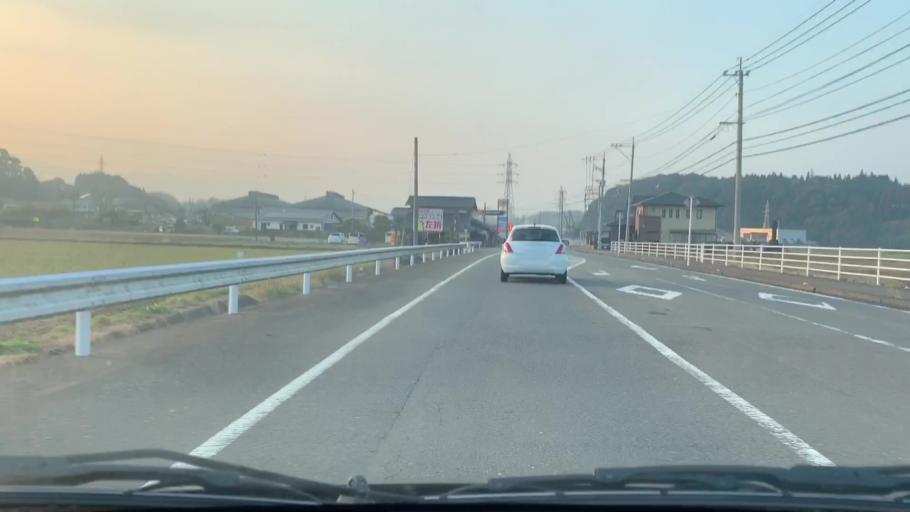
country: JP
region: Saga Prefecture
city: Imaricho-ko
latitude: 33.2687
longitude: 129.8979
